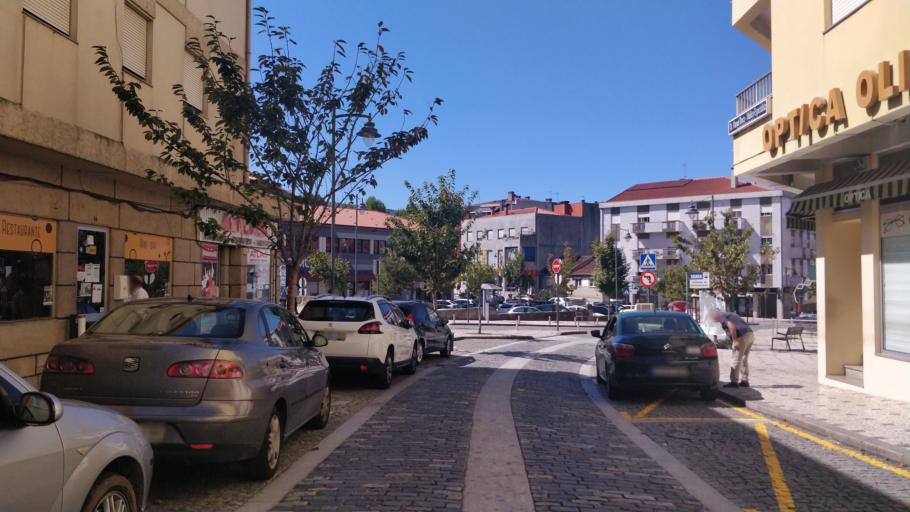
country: PT
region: Viana do Castelo
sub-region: Arcos de Valdevez
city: Mozelos
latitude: 41.8462
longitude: -8.4195
